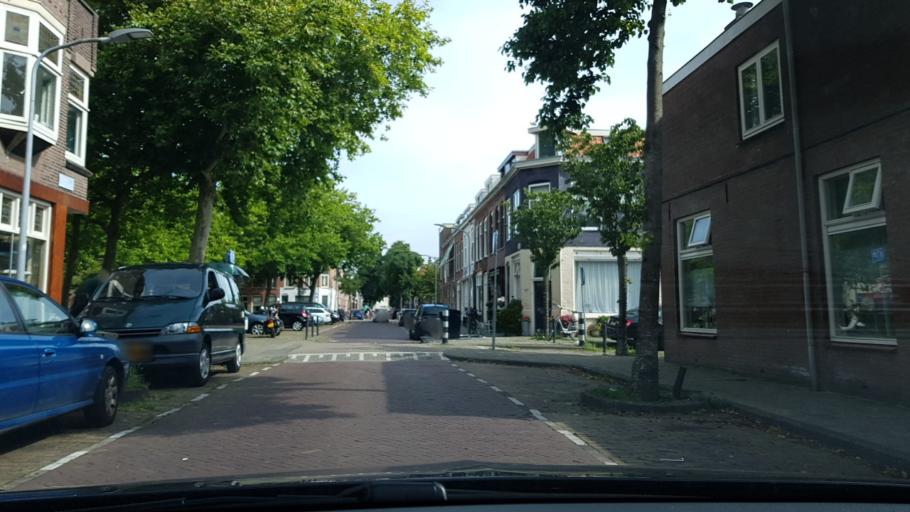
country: NL
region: North Holland
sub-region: Gemeente Haarlem
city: Haarlem
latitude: 52.3928
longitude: 4.6441
